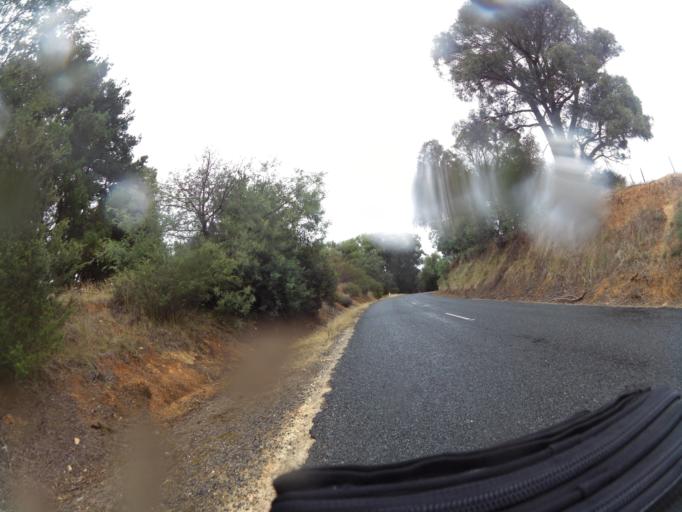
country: AU
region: New South Wales
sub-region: Greater Hume Shire
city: Holbrook
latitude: -36.2348
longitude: 147.6508
